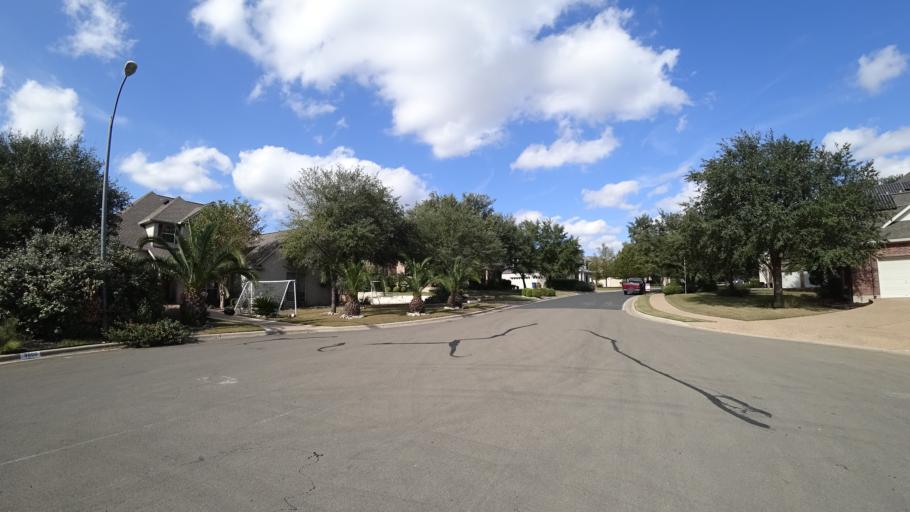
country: US
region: Texas
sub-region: Williamson County
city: Anderson Mill
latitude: 30.4255
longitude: -97.8132
